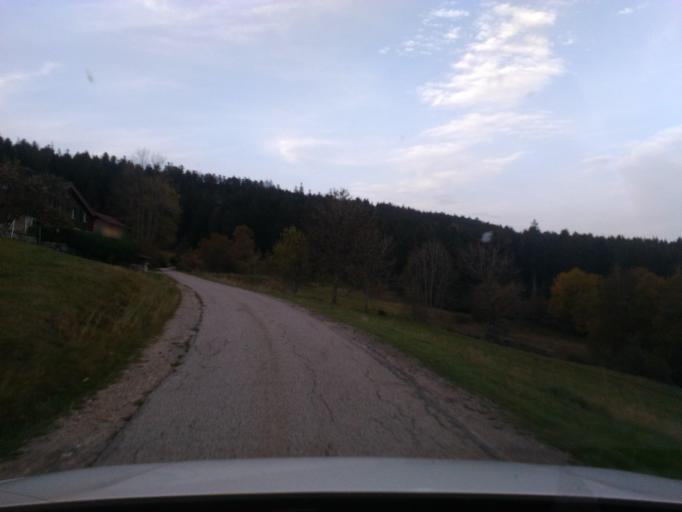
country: FR
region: Lorraine
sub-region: Departement des Vosges
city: Le Tholy
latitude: 48.0887
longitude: 6.7897
